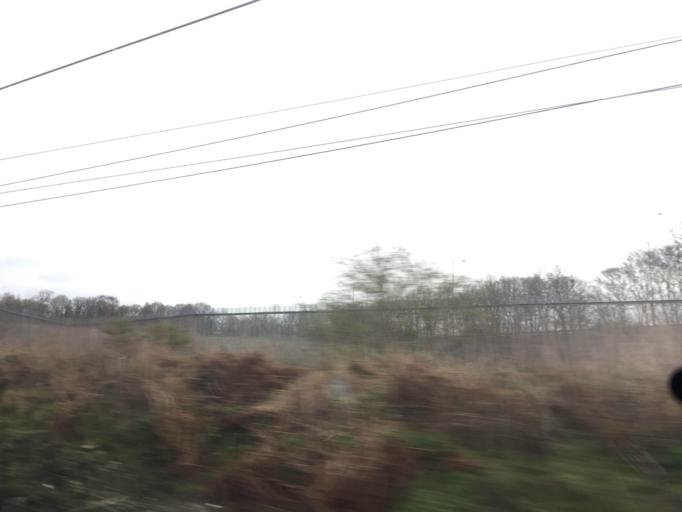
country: GB
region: England
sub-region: Lancashire
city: Leyland
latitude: 53.6855
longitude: -2.6807
